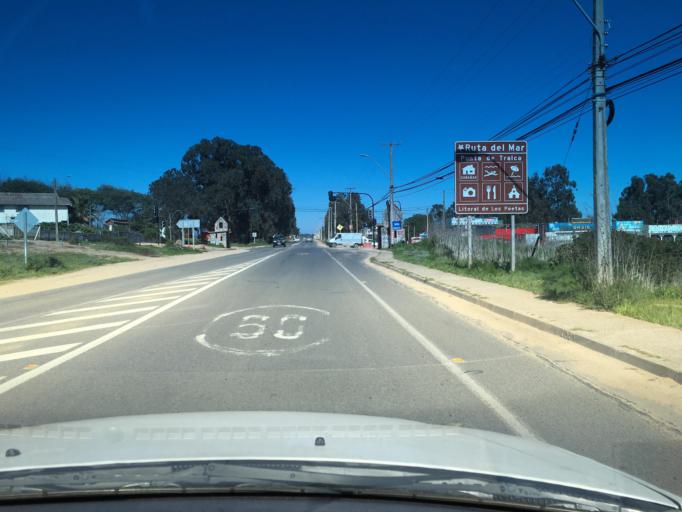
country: CL
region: Valparaiso
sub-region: San Antonio Province
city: El Tabo
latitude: -33.4250
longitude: -71.6921
